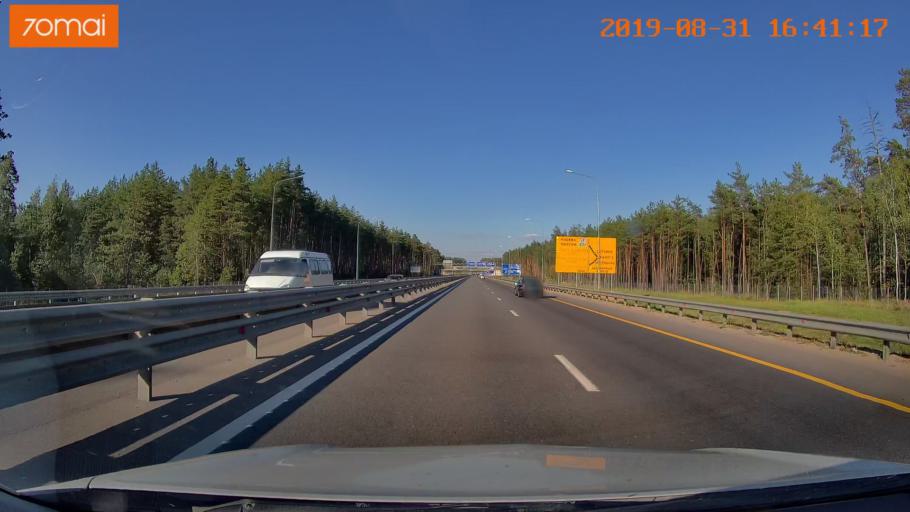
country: RU
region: Kaluga
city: Mstikhino
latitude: 54.5777
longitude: 36.0644
